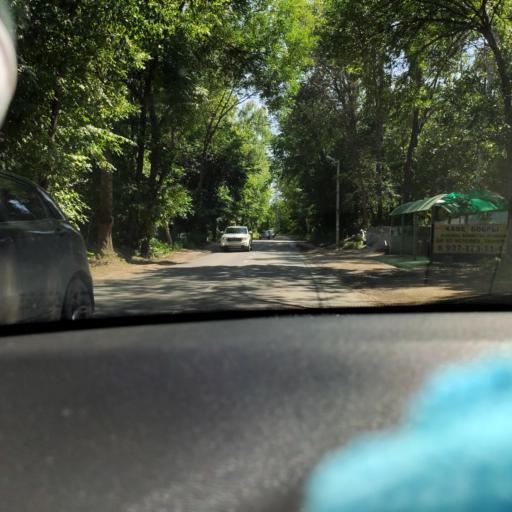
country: RU
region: Samara
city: Novokuybyshevsk
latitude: 53.1548
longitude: 49.9563
